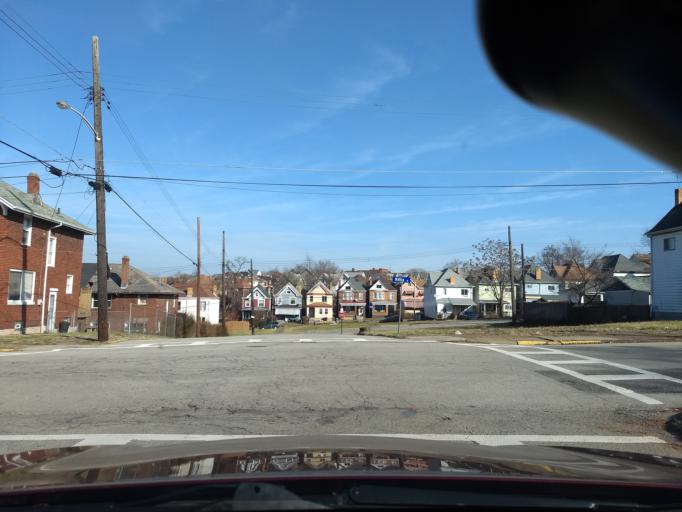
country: US
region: Pennsylvania
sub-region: Allegheny County
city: Homestead
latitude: 40.4036
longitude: -79.9040
